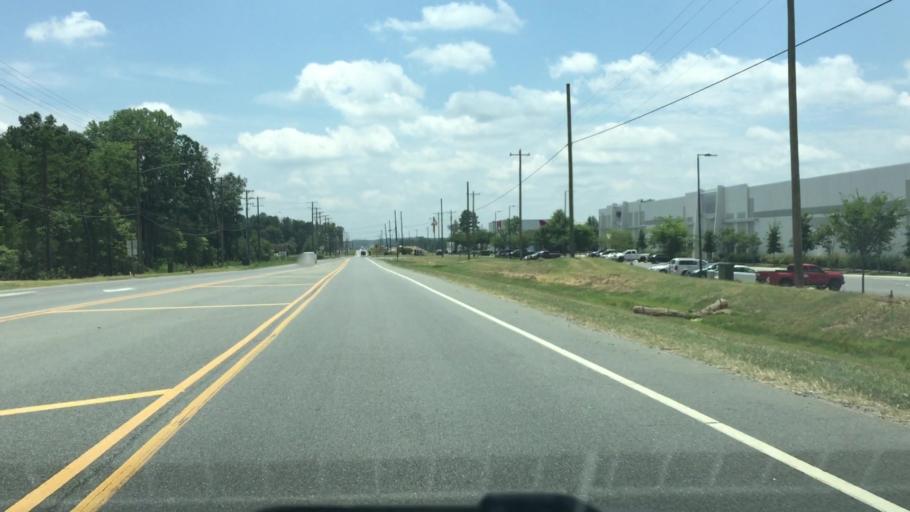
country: US
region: North Carolina
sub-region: Cabarrus County
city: Harrisburg
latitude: 35.4041
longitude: -80.7146
